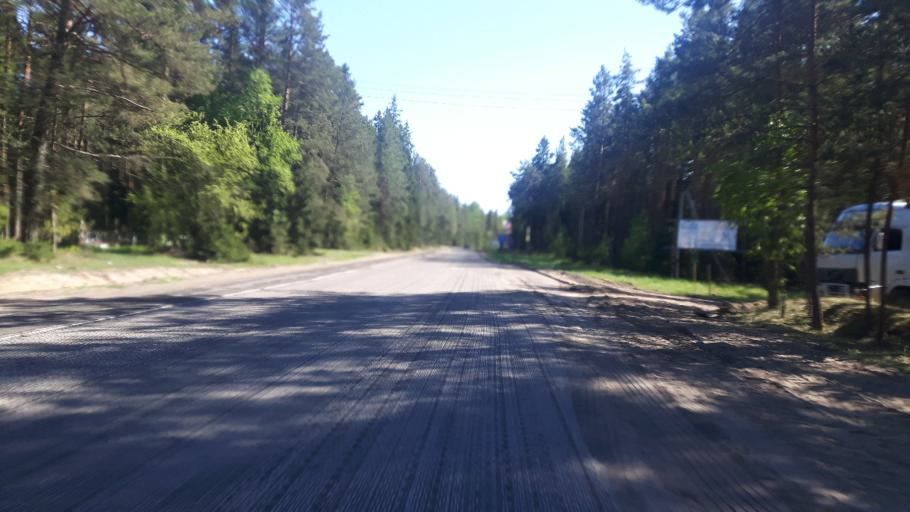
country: RU
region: Leningrad
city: Sosnovyy Bor
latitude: 60.2336
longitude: 29.0007
